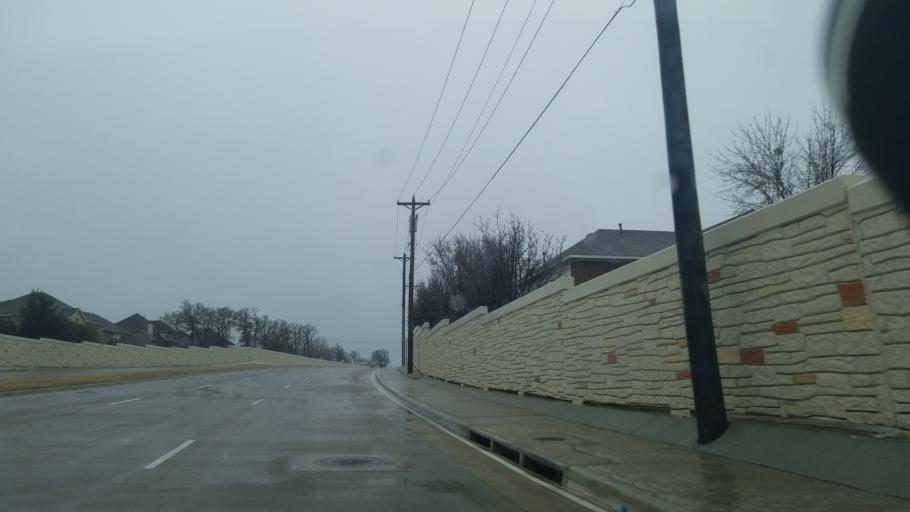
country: US
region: Texas
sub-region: Denton County
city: Corinth
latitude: 33.1602
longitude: -97.0931
